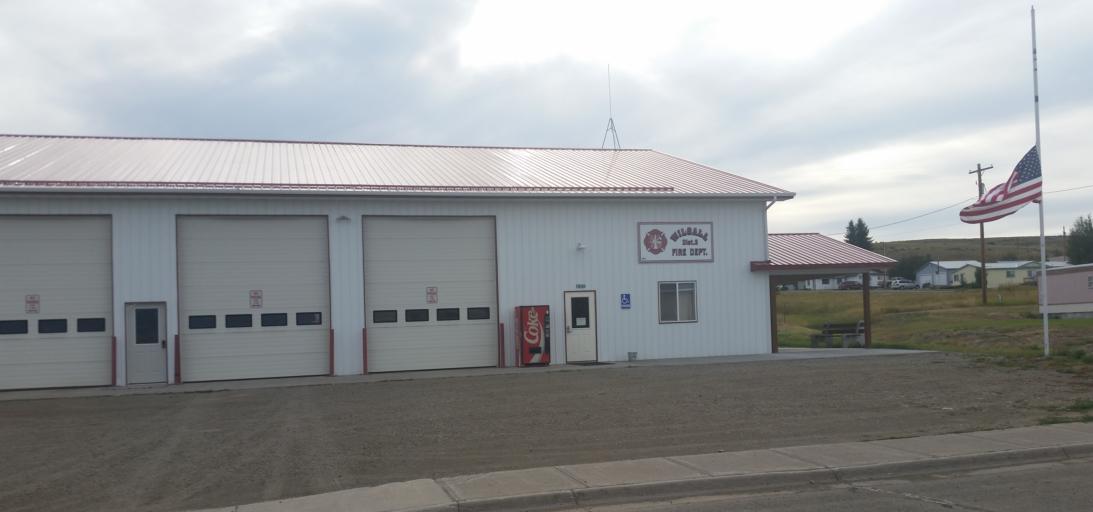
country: US
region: Montana
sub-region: Park County
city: Livingston
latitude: 45.9950
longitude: -110.6606
